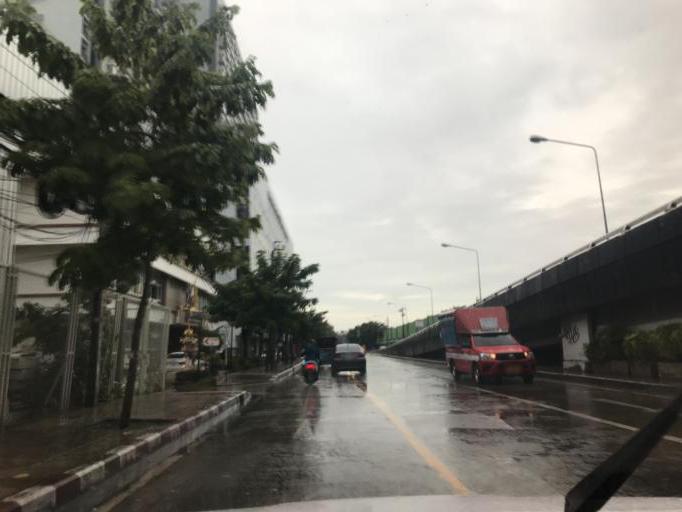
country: TH
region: Bangkok
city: Bangkok Noi
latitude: 13.7597
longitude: 100.4818
